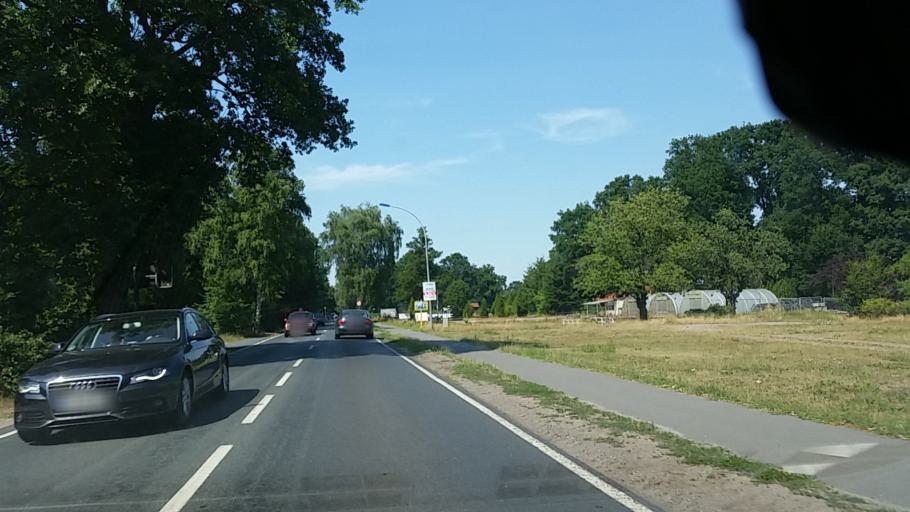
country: DE
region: Lower Saxony
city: Ottersberg
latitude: 53.0614
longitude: 9.1717
